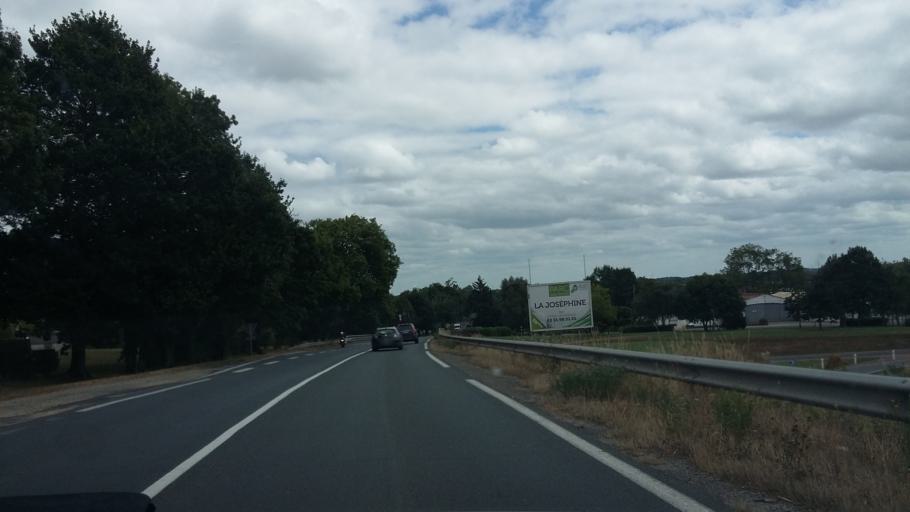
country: FR
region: Pays de la Loire
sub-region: Departement de la Vendee
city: Saint-Christophe-du-Ligneron
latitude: 46.8211
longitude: -1.7664
